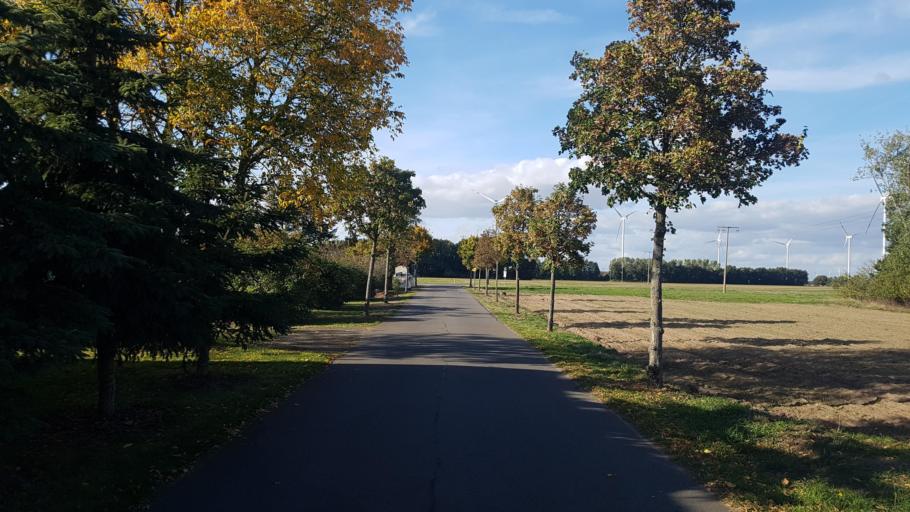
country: DE
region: Saxony
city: Nauwalde
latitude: 51.4567
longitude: 13.3378
